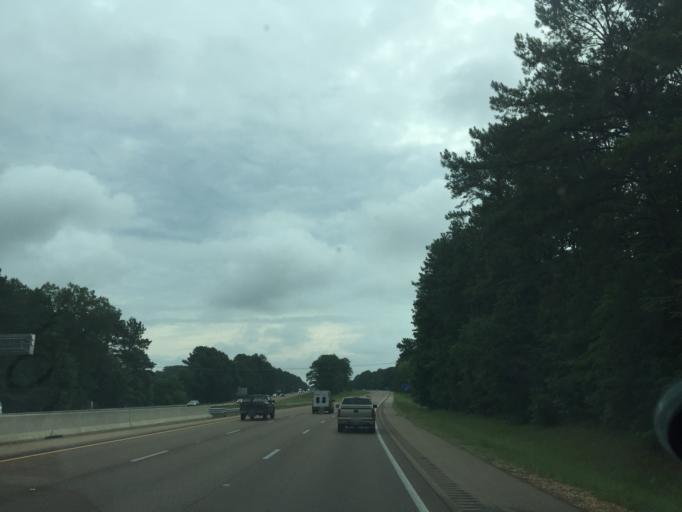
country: US
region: Mississippi
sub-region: Rankin County
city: Brandon
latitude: 32.2736
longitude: -90.0589
